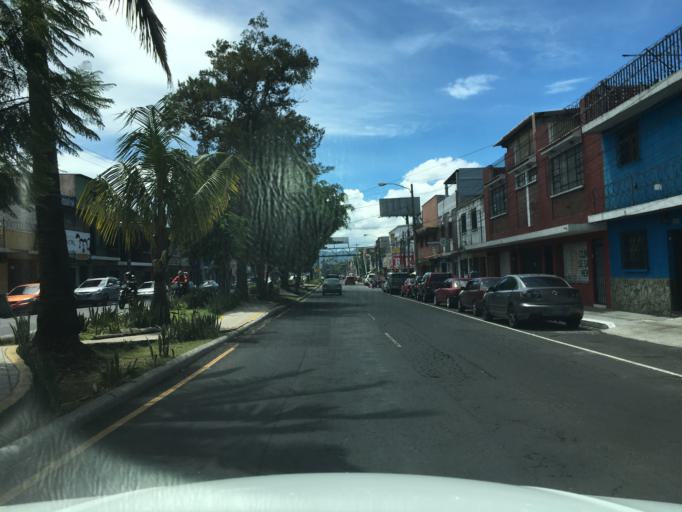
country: GT
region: Guatemala
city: Guatemala City
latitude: 14.6269
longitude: -90.5437
